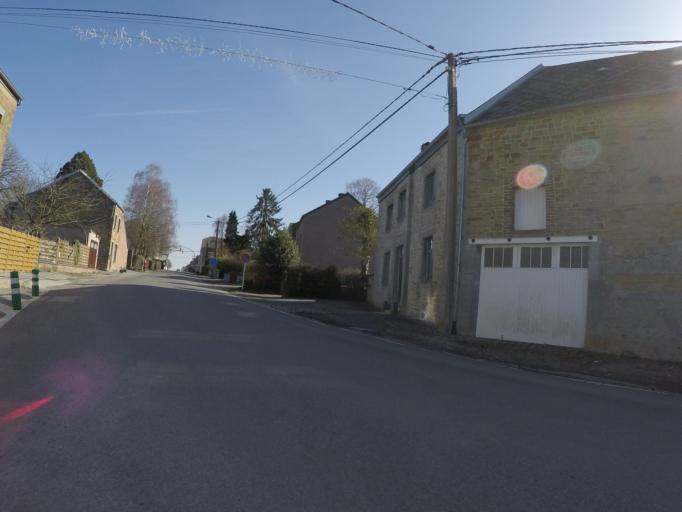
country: BE
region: Wallonia
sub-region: Province de Namur
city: Havelange
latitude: 50.3903
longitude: 5.2365
